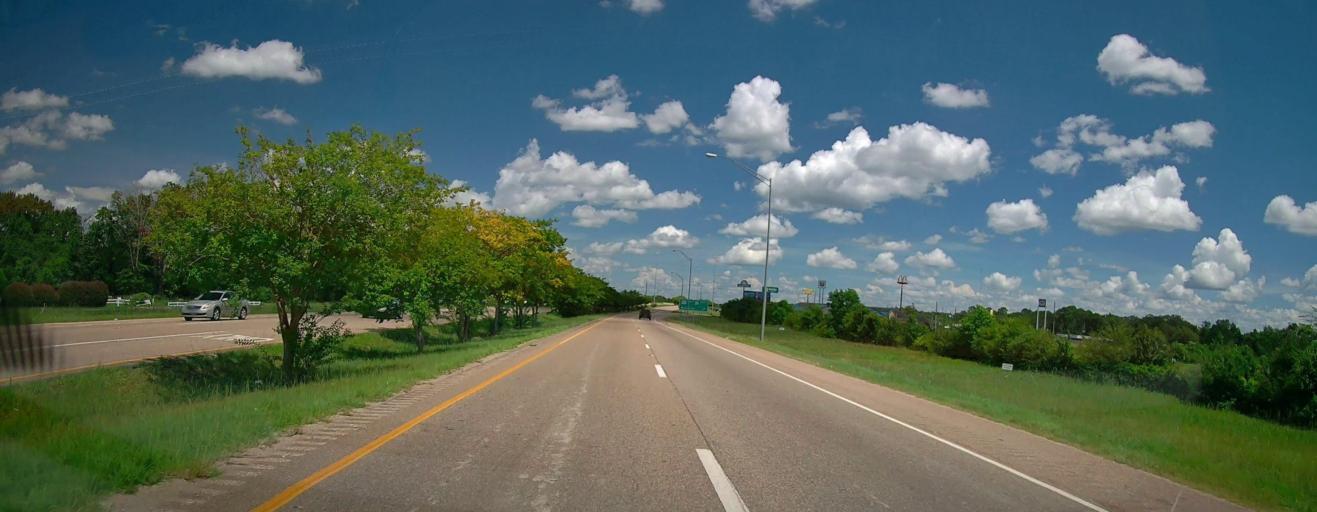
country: US
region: Alabama
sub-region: Montgomery County
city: Montgomery
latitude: 32.4218
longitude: -86.2362
